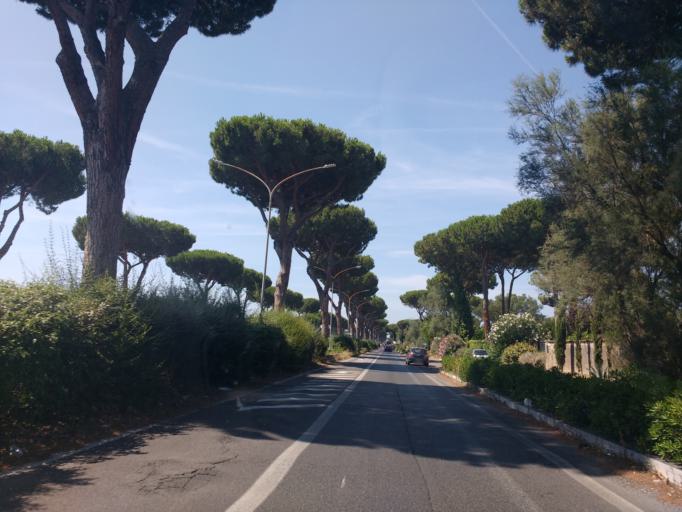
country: IT
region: Latium
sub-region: Citta metropolitana di Roma Capitale
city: Acilia-Castel Fusano-Ostia Antica
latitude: 41.7392
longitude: 12.3491
